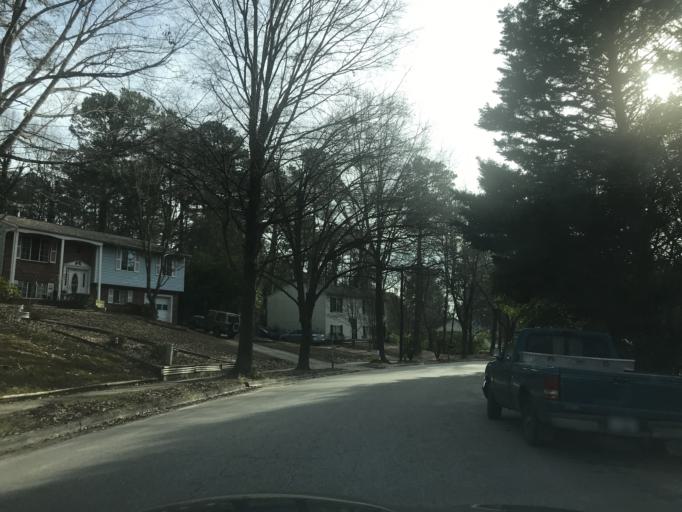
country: US
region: North Carolina
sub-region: Wake County
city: Raleigh
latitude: 35.8281
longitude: -78.5907
